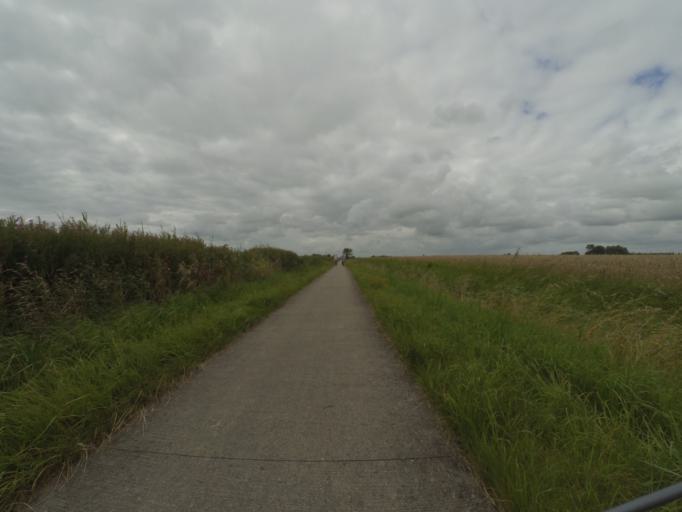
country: NL
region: Friesland
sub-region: Gemeente Kollumerland en Nieuwkruisland
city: Kollum
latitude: 53.3171
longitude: 6.1333
